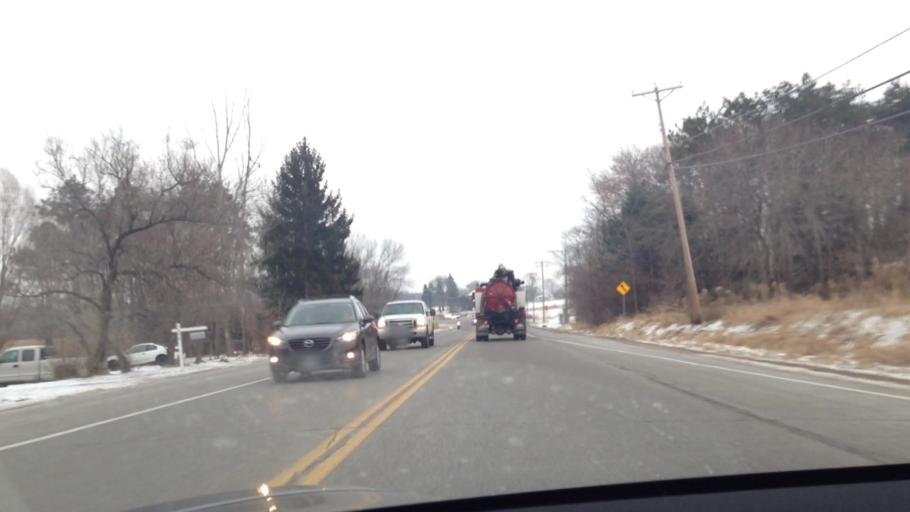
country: US
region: Minnesota
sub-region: Washington County
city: Forest Lake
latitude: 45.2527
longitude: -93.0037
